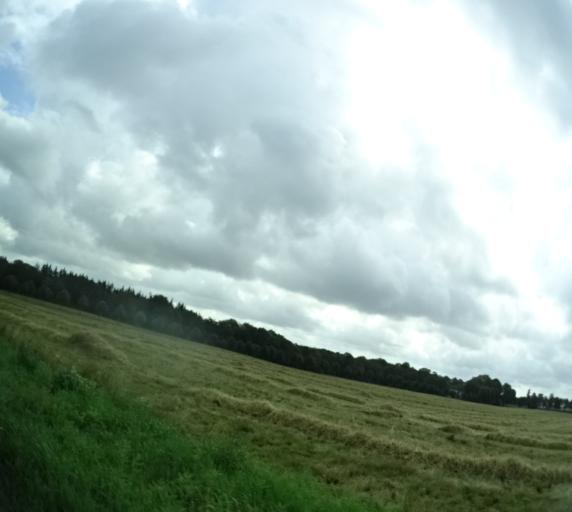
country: DK
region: Central Jutland
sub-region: Syddjurs Kommune
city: Ryomgard
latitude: 56.3945
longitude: 10.5151
